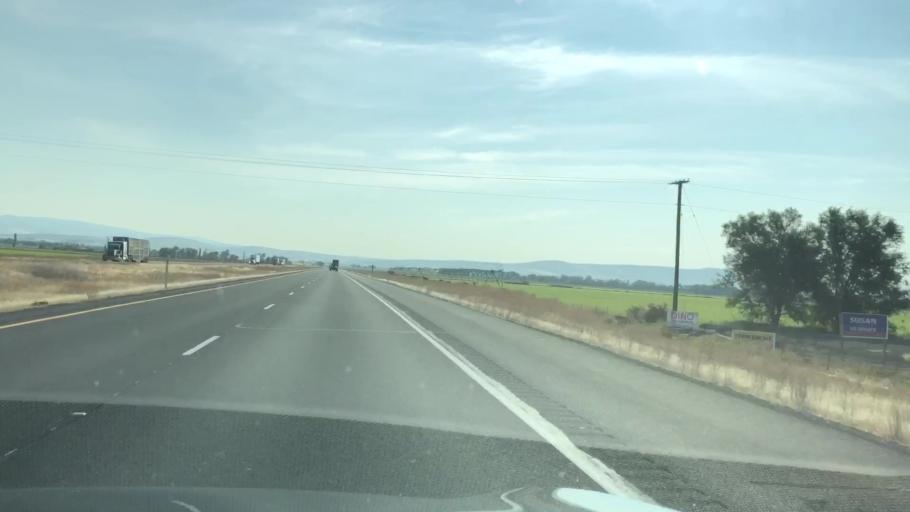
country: US
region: Washington
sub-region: Kittitas County
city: Kittitas
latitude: 46.9687
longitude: -120.4666
